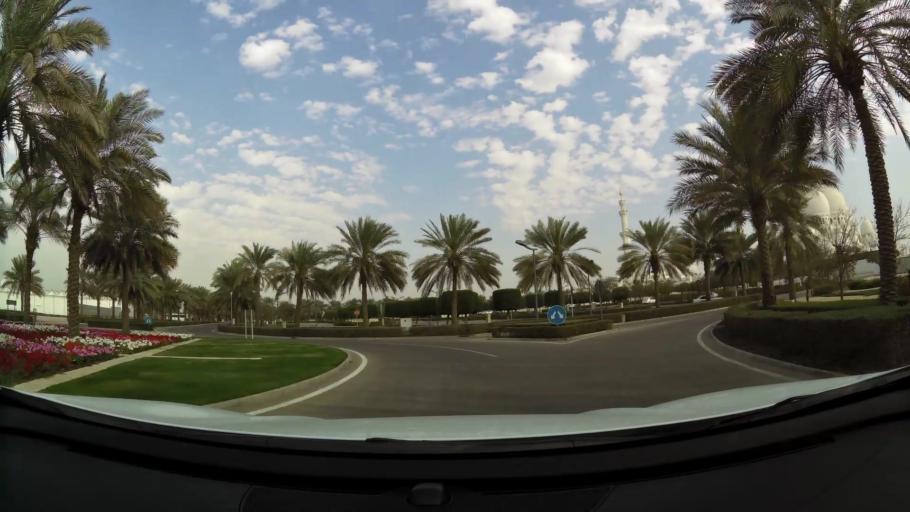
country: AE
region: Abu Dhabi
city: Abu Dhabi
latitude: 24.4154
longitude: 54.4725
